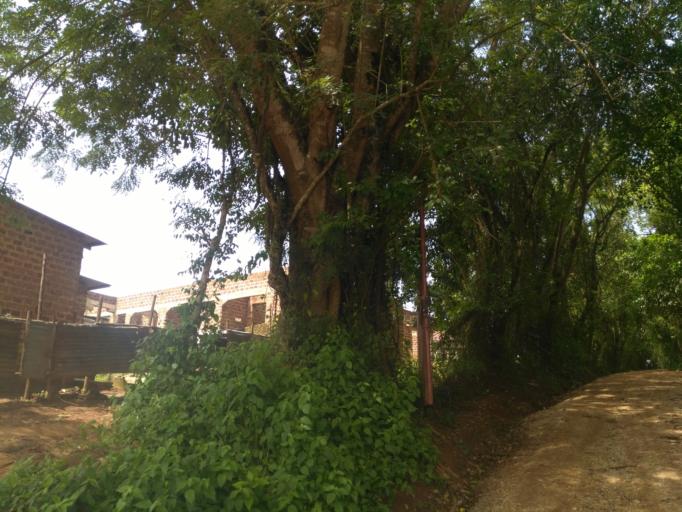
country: UG
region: Central Region
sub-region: Wakiso District
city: Bweyogerere
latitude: 0.4905
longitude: 32.6112
